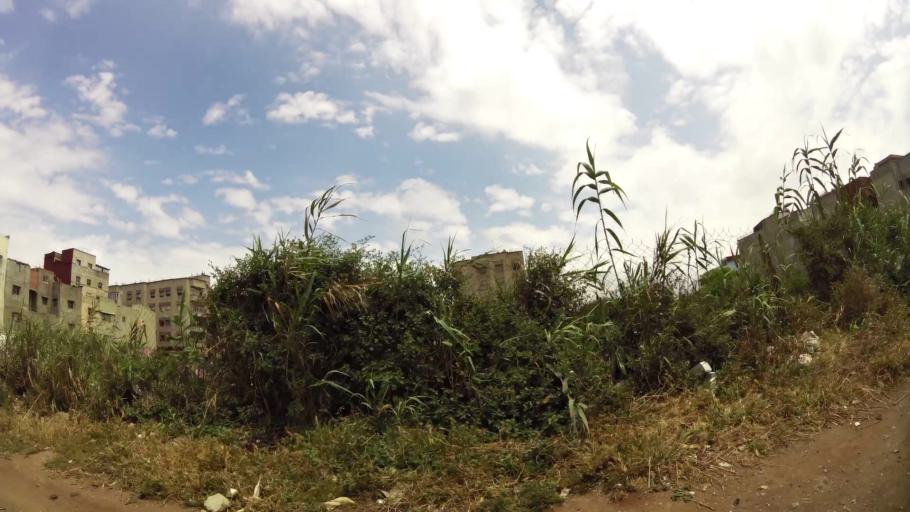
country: MA
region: Rabat-Sale-Zemmour-Zaer
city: Sale
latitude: 34.0527
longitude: -6.8171
